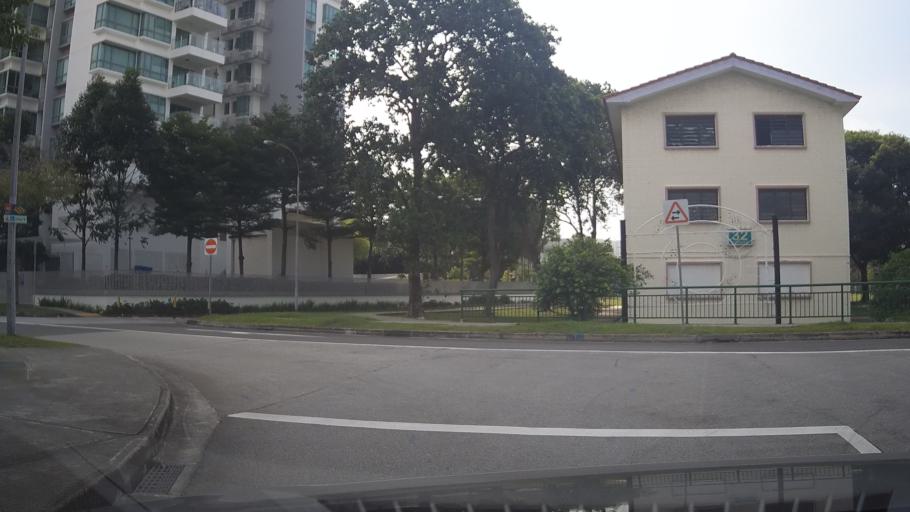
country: SG
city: Singapore
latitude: 1.3069
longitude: 103.8861
